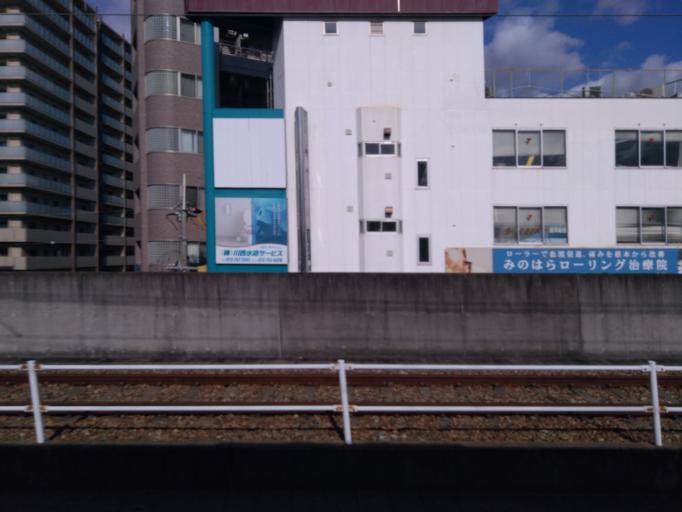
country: JP
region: Hyogo
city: Kawanishi
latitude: 34.8271
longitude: 135.4159
